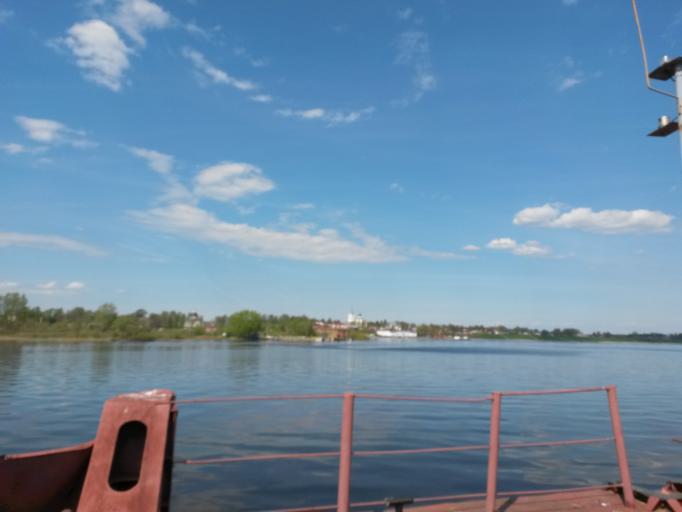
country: RU
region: Jaroslavl
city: Myshkin
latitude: 57.7772
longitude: 38.4546
